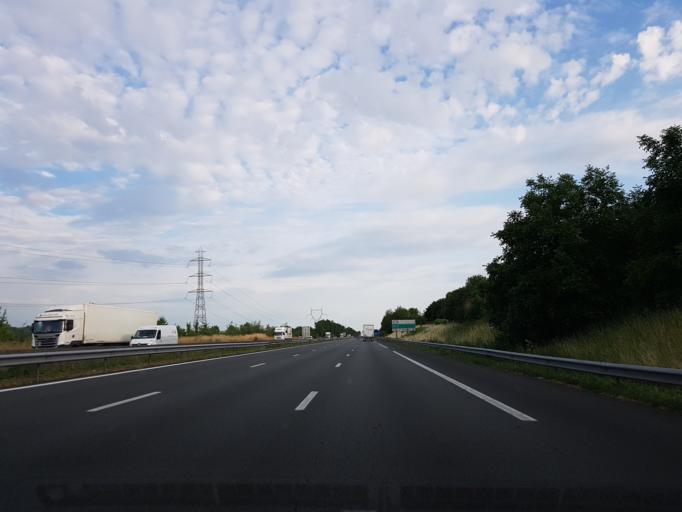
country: FR
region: Picardie
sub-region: Departement de l'Oise
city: Longueil-Sainte-Marie
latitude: 49.3883
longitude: 2.7004
